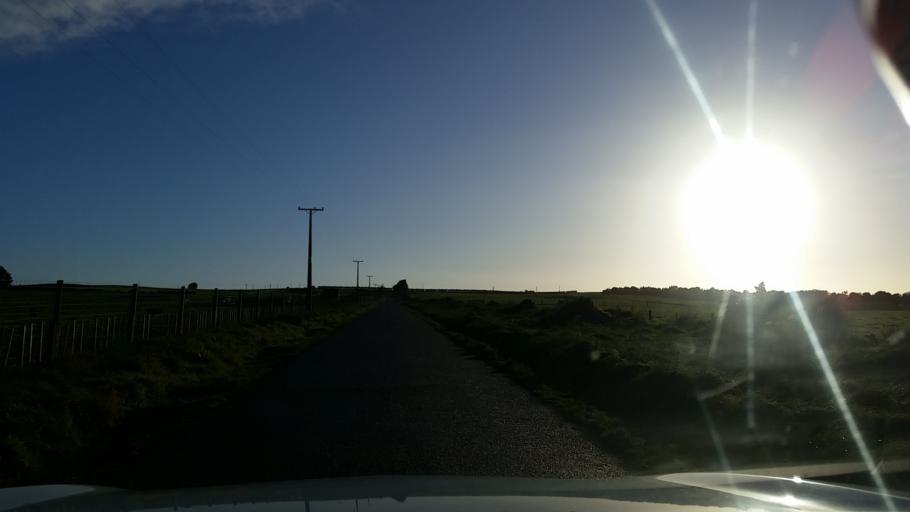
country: NZ
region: Manawatu-Wanganui
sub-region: Wanganui District
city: Wanganui
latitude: -39.8198
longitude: 174.7941
